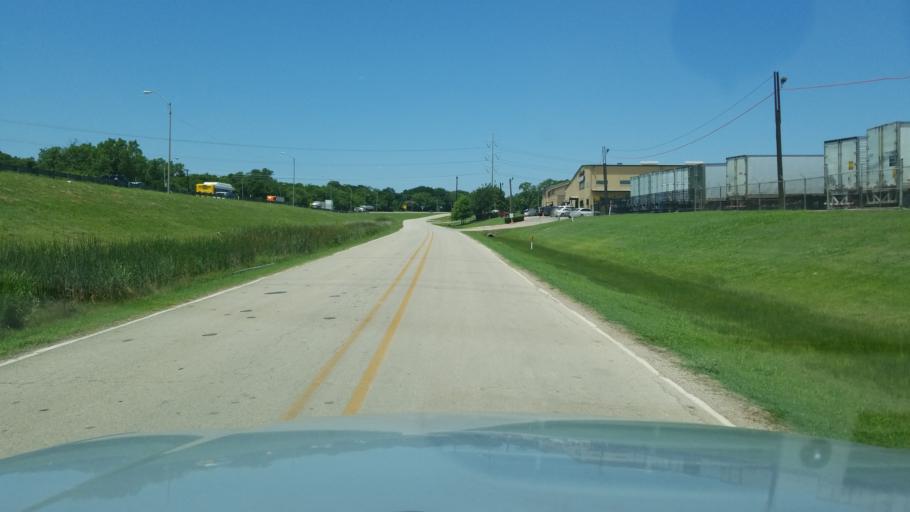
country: US
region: Texas
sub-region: Dallas County
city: Irving
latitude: 32.8096
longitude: -96.9100
